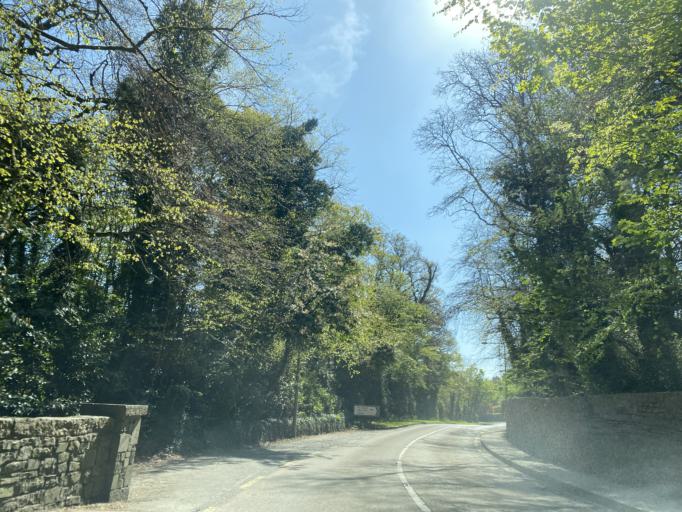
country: IE
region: Leinster
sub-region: Kildare
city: Kill
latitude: 53.3047
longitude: -6.6148
